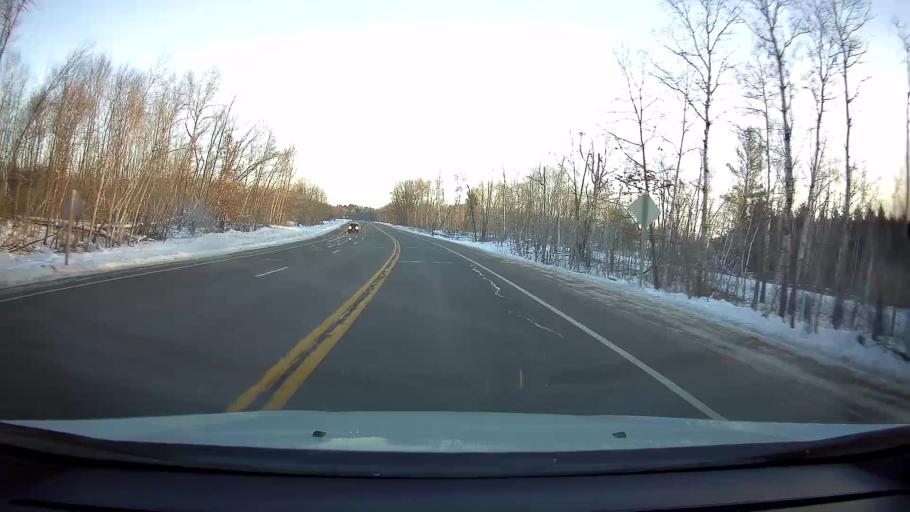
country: US
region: Wisconsin
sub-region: Barron County
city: Turtle Lake
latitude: 45.4490
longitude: -92.1088
